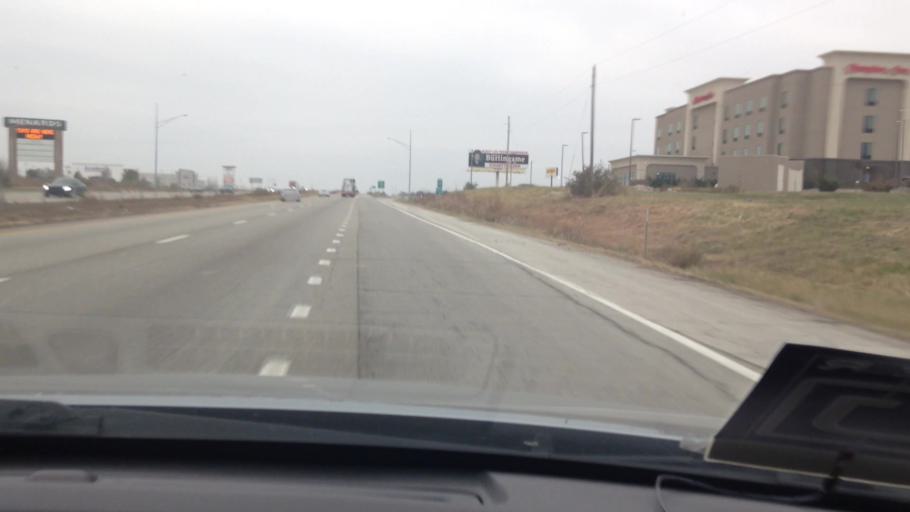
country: US
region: Missouri
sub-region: Cass County
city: Belton
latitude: 38.8225
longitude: -94.5163
